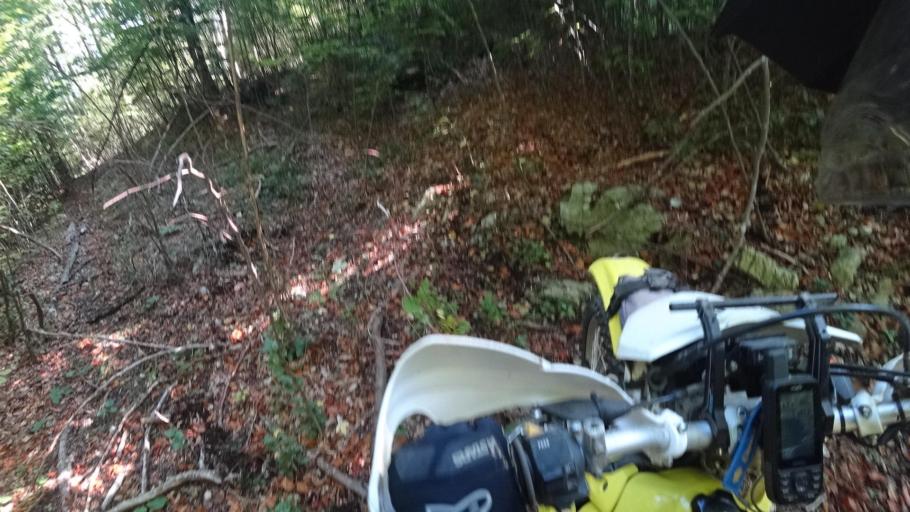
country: HR
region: Primorsko-Goranska
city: Vrbovsko
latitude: 45.2996
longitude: 15.1288
